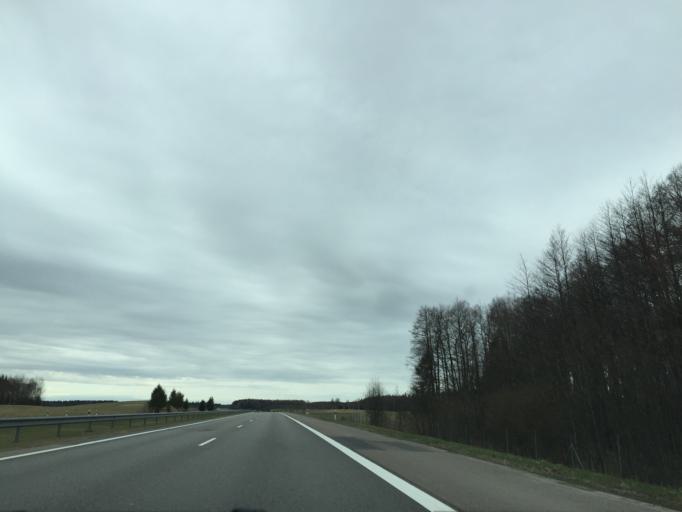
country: LT
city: Rietavas
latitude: 55.6569
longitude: 21.7778
